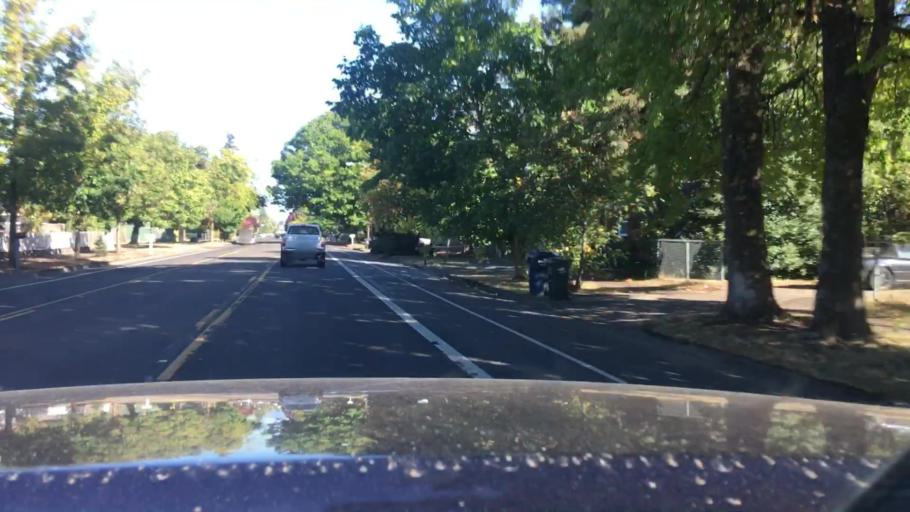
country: US
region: Oregon
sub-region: Lane County
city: Eugene
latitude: 44.0696
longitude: -123.0620
